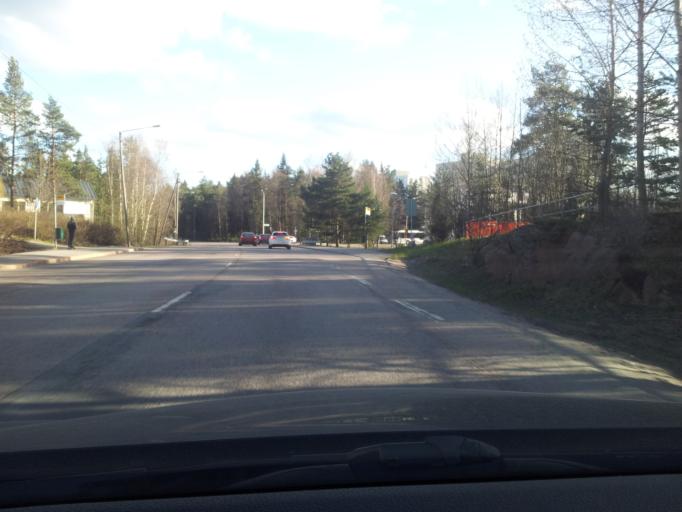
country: FI
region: Uusimaa
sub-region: Helsinki
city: Espoo
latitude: 60.1389
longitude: 24.6772
